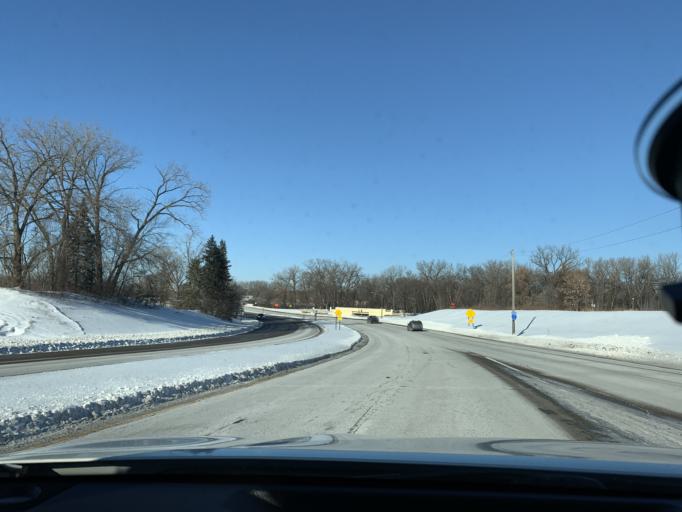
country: US
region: Minnesota
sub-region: Anoka County
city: Coon Rapids
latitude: 45.1498
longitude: -93.2950
